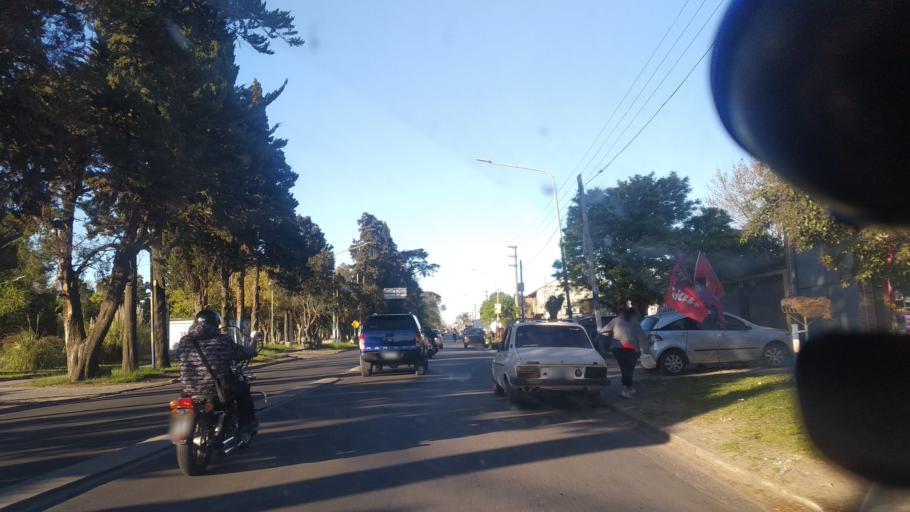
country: AR
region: Buenos Aires
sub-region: Partido de La Plata
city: La Plata
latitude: -34.9677
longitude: -57.9808
